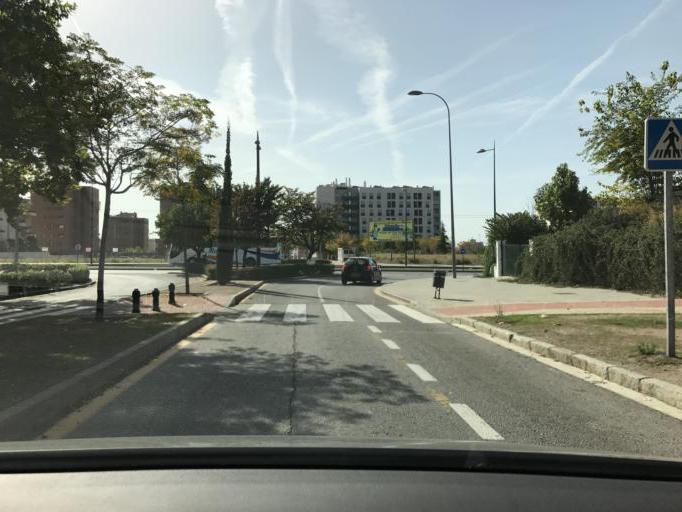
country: ES
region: Andalusia
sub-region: Provincia de Granada
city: Granada
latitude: 37.2036
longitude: -3.6159
